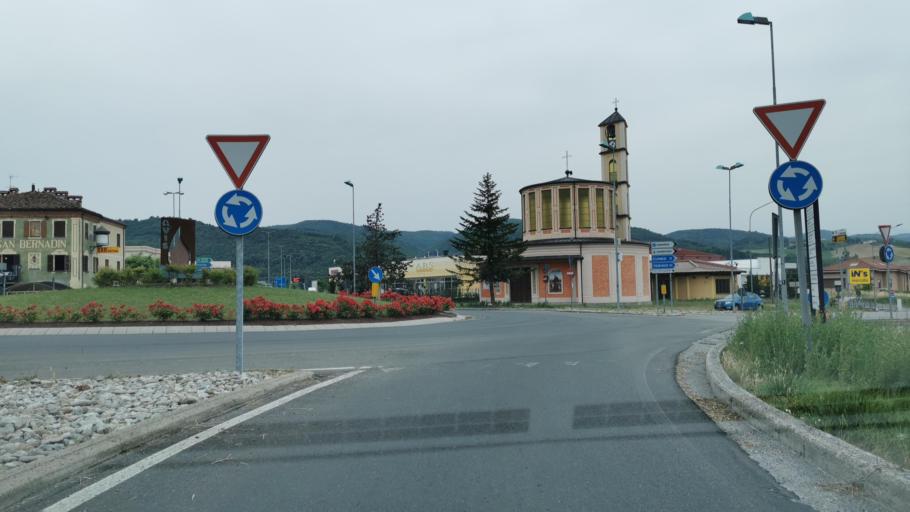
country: IT
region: Piedmont
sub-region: Provincia di Cuneo
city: Ceva
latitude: 44.3778
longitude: 8.0412
